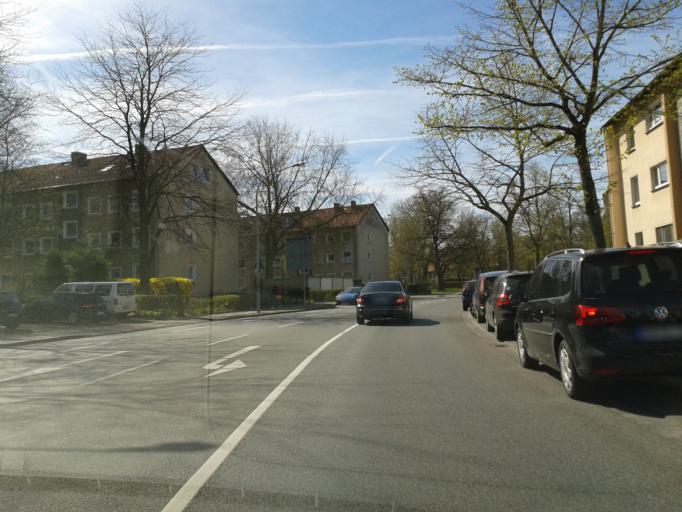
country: DE
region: Lower Saxony
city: Uelzen
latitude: 52.9635
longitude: 10.5753
